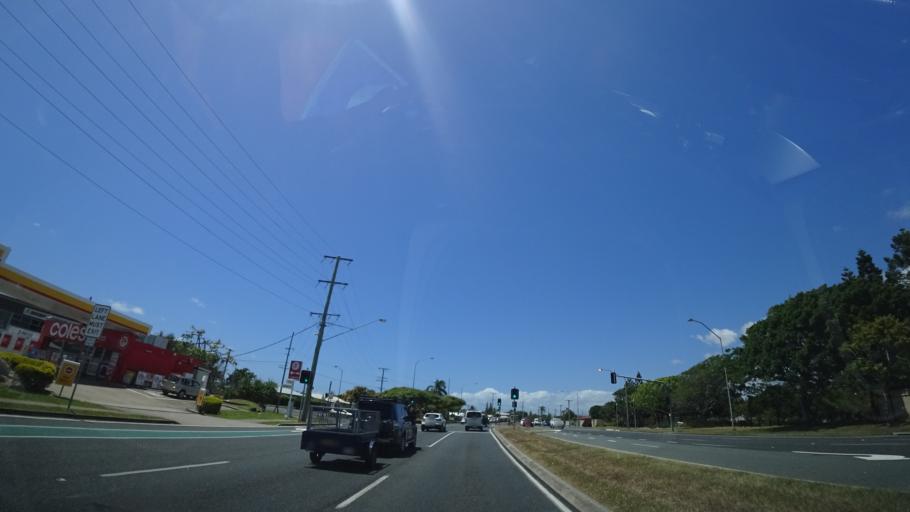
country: AU
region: Queensland
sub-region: Sunshine Coast
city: Mooloolaba
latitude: -26.7049
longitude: 153.1298
